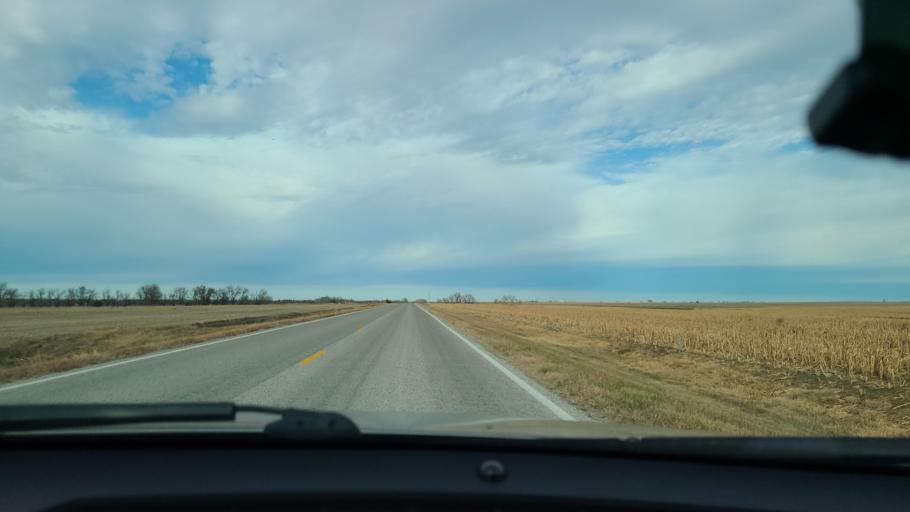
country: US
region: Kansas
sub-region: McPherson County
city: Inman
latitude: 38.3304
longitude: -97.9246
